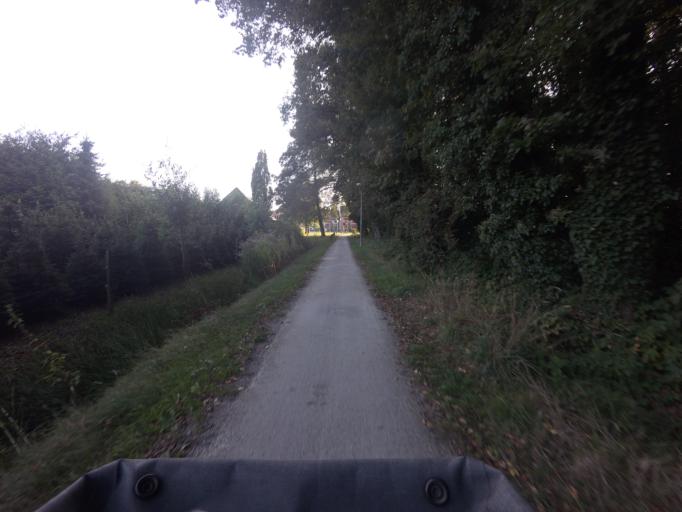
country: NL
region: Groningen
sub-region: Gemeente Haren
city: Haren
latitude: 53.1492
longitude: 6.5647
